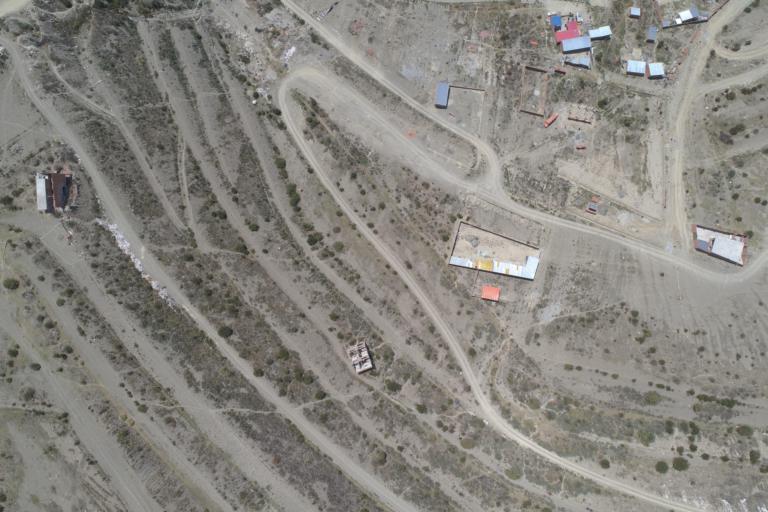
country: BO
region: La Paz
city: La Paz
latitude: -16.5032
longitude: -68.0984
